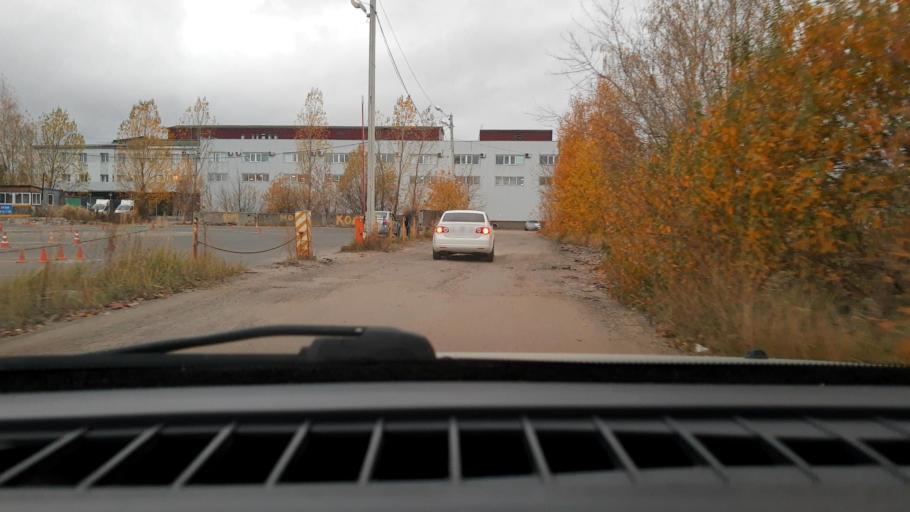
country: RU
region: Nizjnij Novgorod
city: Nizhniy Novgorod
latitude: 56.3342
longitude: 43.8987
